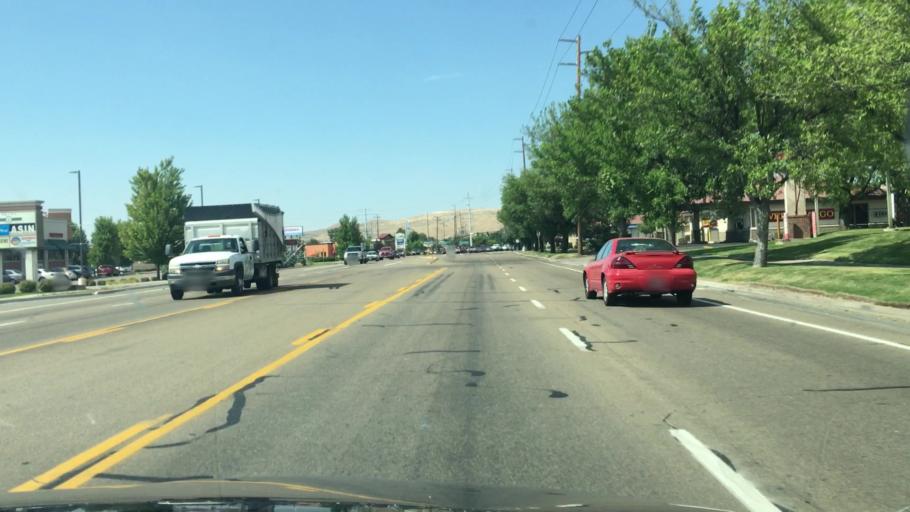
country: US
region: Idaho
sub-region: Ada County
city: Garden City
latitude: 43.6655
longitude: -116.2793
